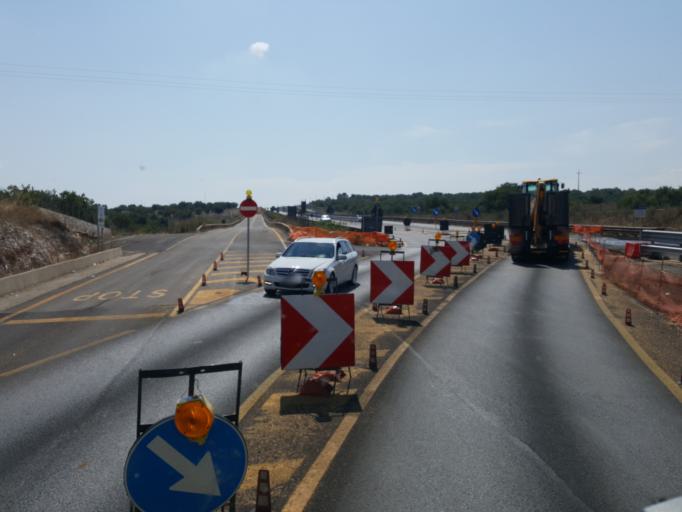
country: IT
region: Apulia
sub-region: Provincia di Bari
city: Quasano
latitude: 40.9240
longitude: 16.6327
